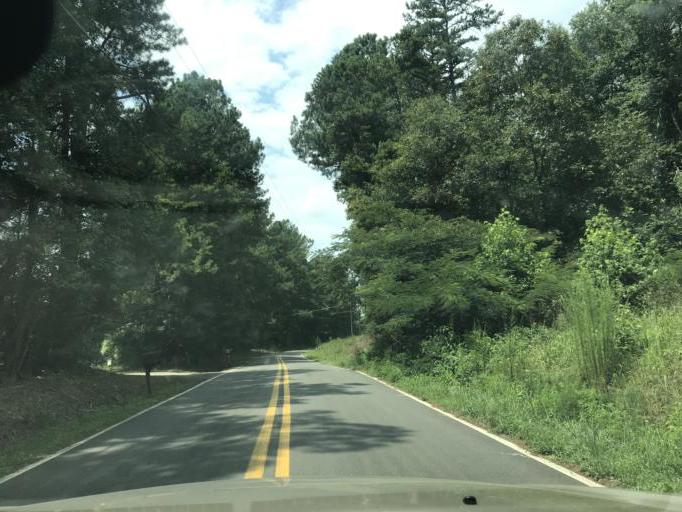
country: US
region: Georgia
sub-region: Dawson County
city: Dawsonville
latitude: 34.3313
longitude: -84.2002
